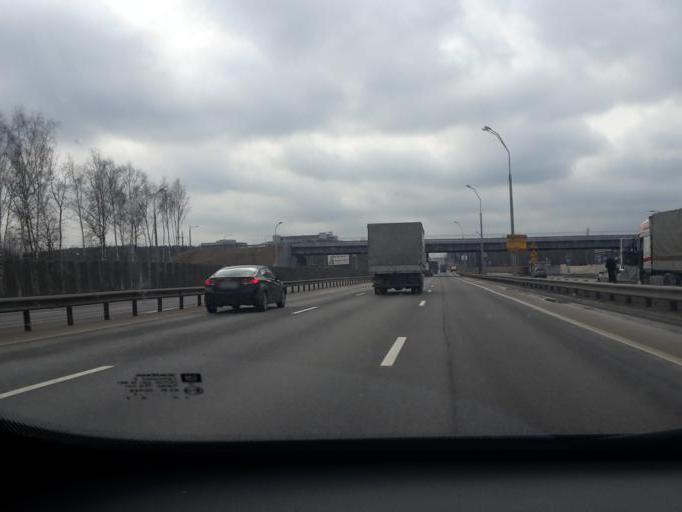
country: BY
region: Minsk
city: Borovlyany
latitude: 53.9369
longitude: 27.6747
